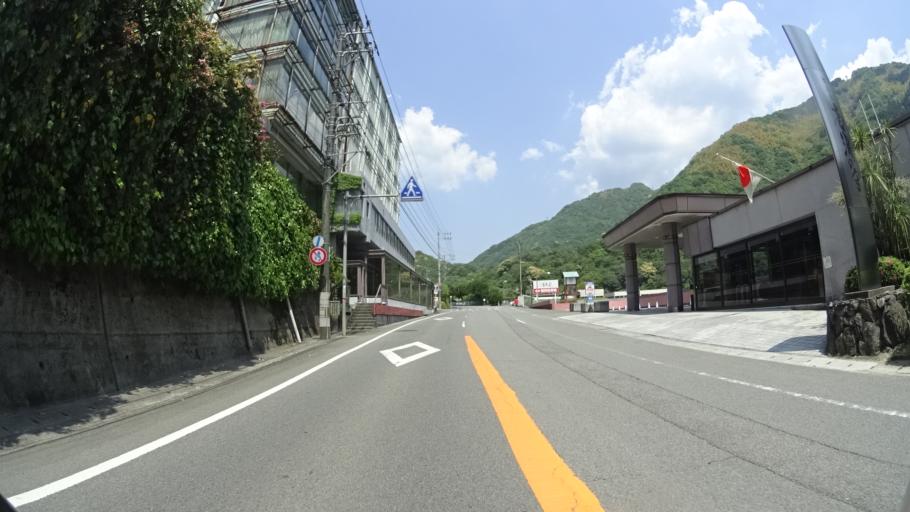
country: JP
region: Ehime
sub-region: Shikoku-chuo Shi
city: Matsuyama
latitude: 33.8661
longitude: 132.8252
